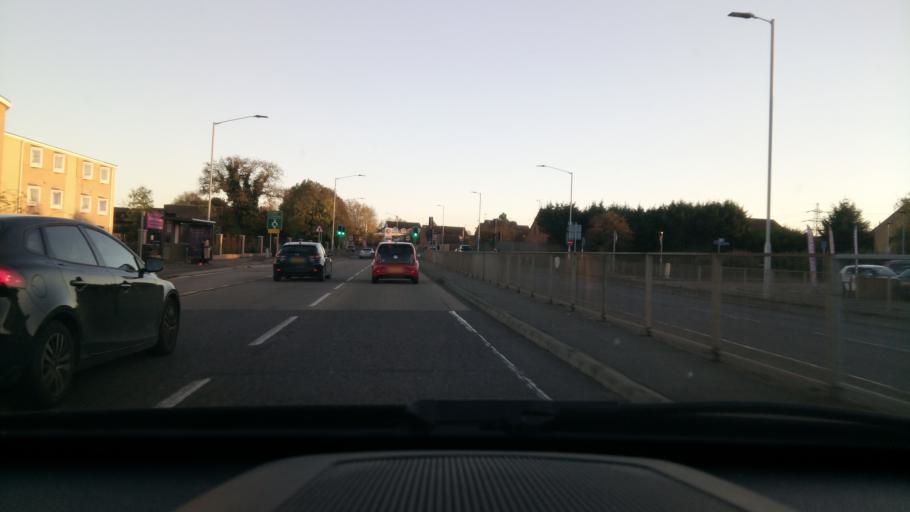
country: GB
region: England
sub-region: Peterborough
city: Marholm
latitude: 52.6061
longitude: -0.2724
